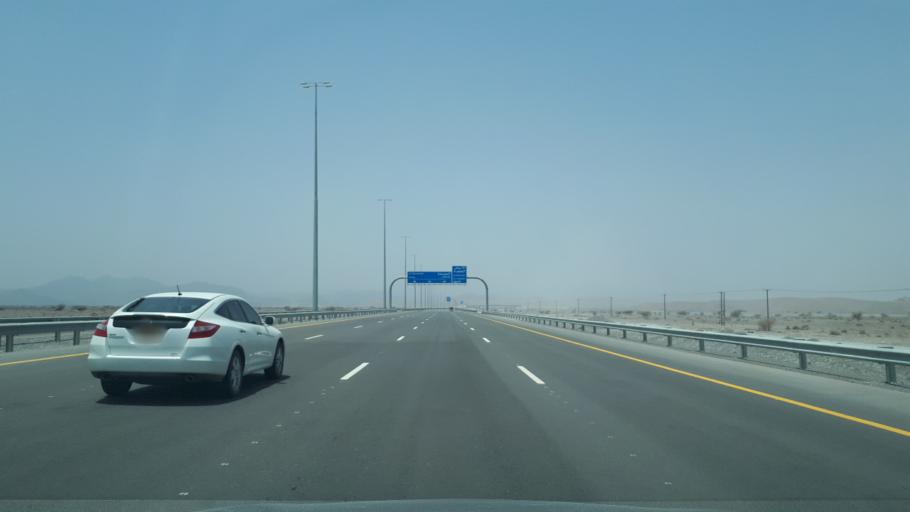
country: OM
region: Al Batinah
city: Barka'
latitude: 23.5392
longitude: 57.6757
